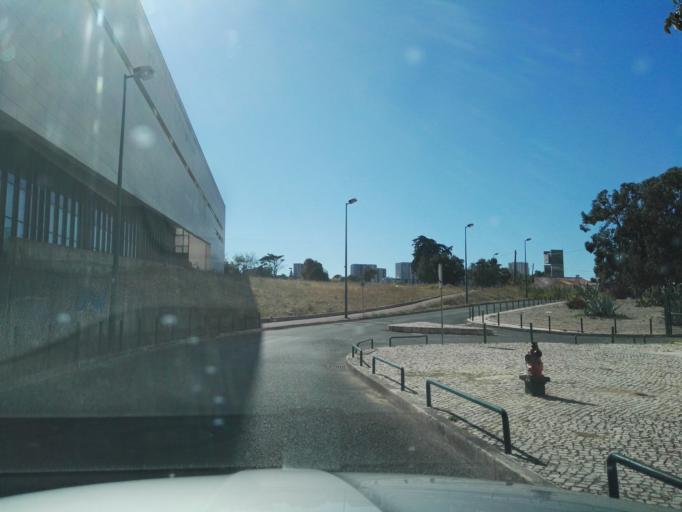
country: PT
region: Lisbon
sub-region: Odivelas
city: Olival do Basto
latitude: 38.7551
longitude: -9.1577
